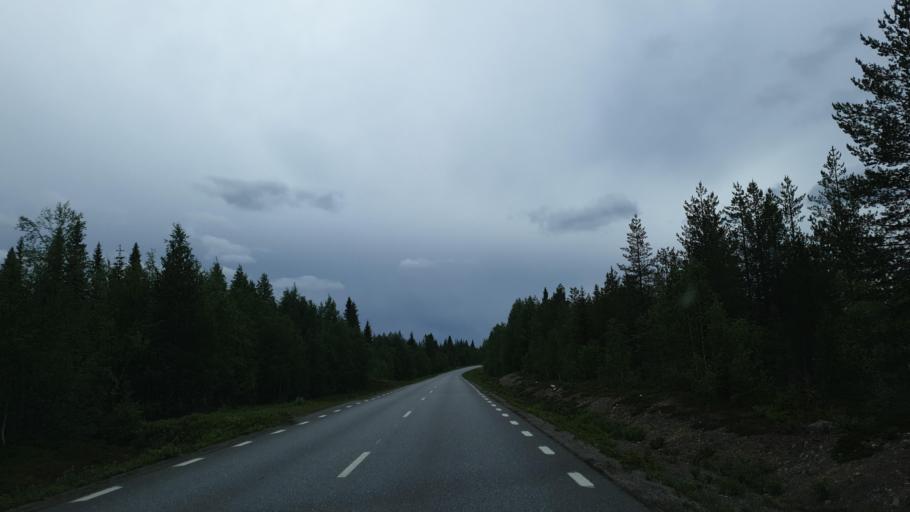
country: SE
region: Vaesterbotten
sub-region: Sorsele Kommun
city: Sorsele
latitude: 65.5118
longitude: 17.3059
